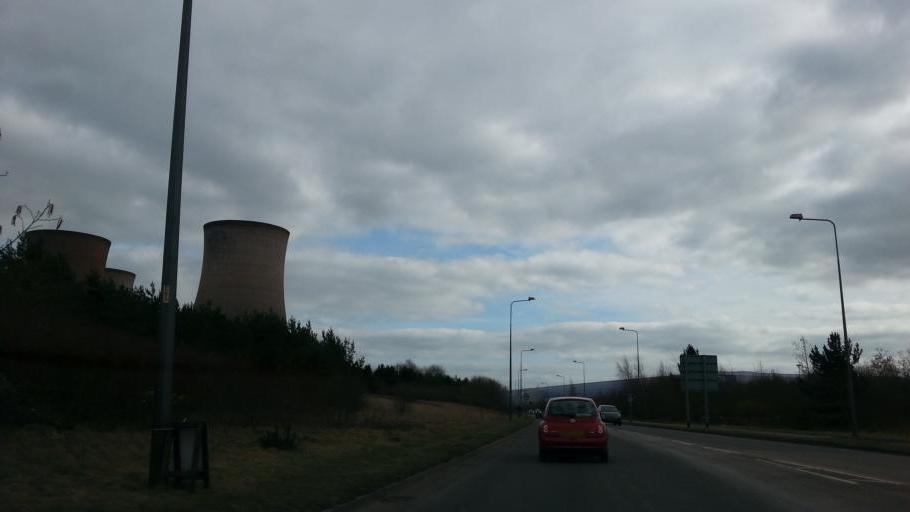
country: GB
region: England
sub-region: Staffordshire
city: Rugeley
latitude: 52.7578
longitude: -1.9250
